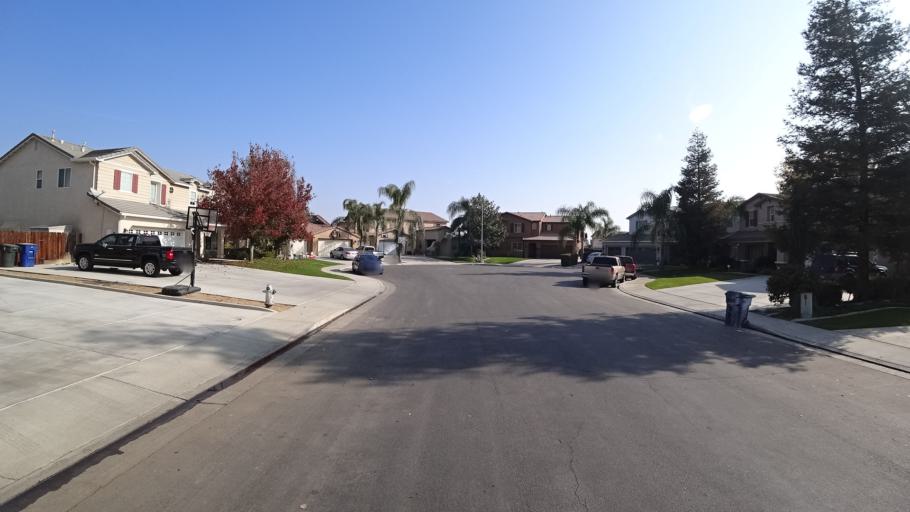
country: US
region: California
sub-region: Kern County
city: Greenacres
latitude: 35.4145
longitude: -119.1254
